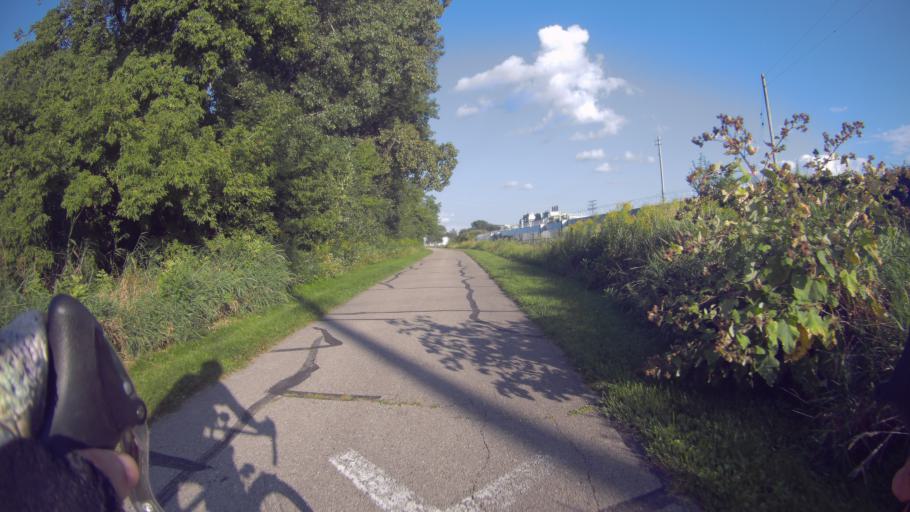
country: US
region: Wisconsin
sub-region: Dane County
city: Monona
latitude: 43.0392
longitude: -89.3591
